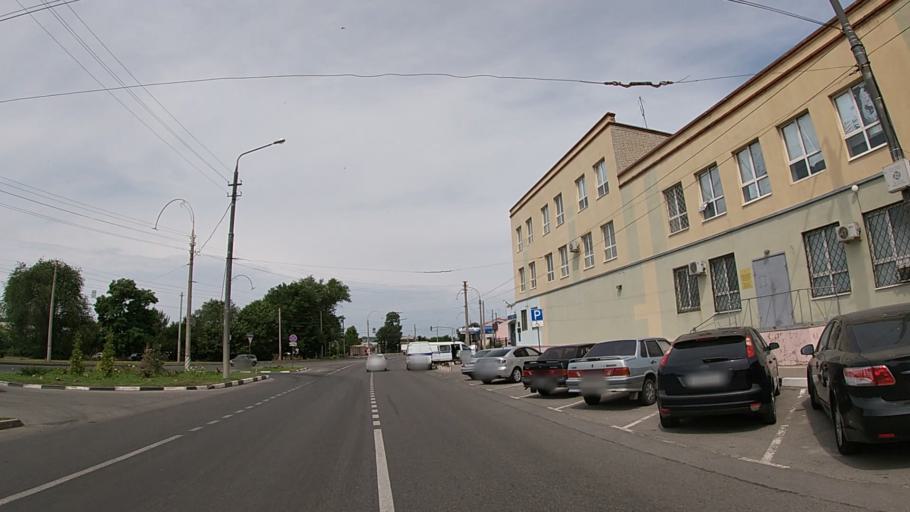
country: RU
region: Belgorod
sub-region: Belgorodskiy Rayon
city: Belgorod
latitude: 50.6023
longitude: 36.5627
